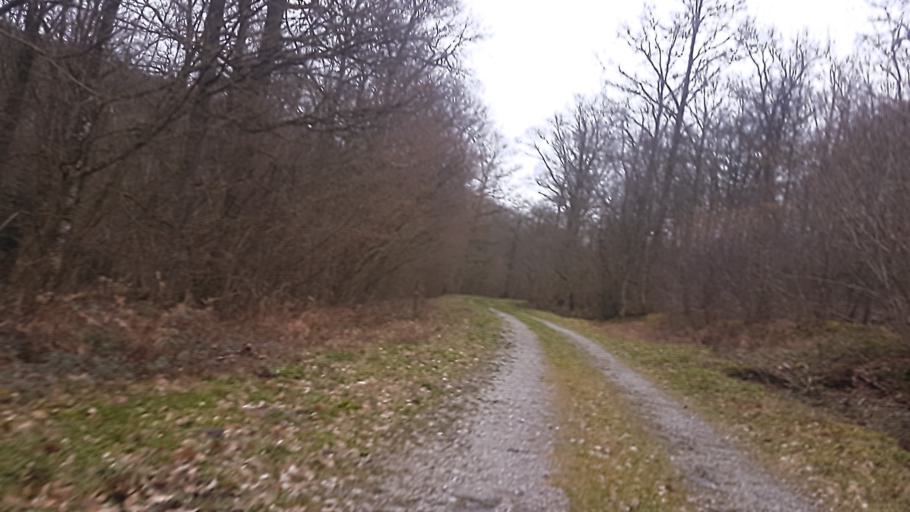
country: FR
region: Champagne-Ardenne
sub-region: Departement des Ardennes
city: Haybes
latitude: 50.0476
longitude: 4.6207
